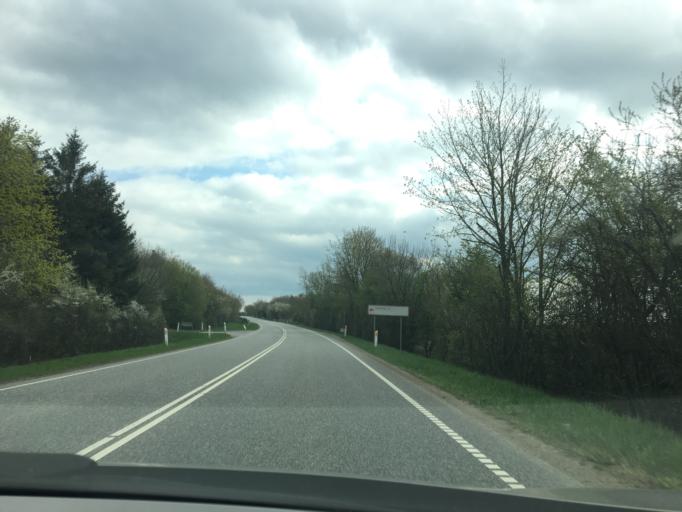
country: DK
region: Central Jutland
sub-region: Horsens Kommune
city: Braedstrup
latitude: 55.9670
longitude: 9.6038
